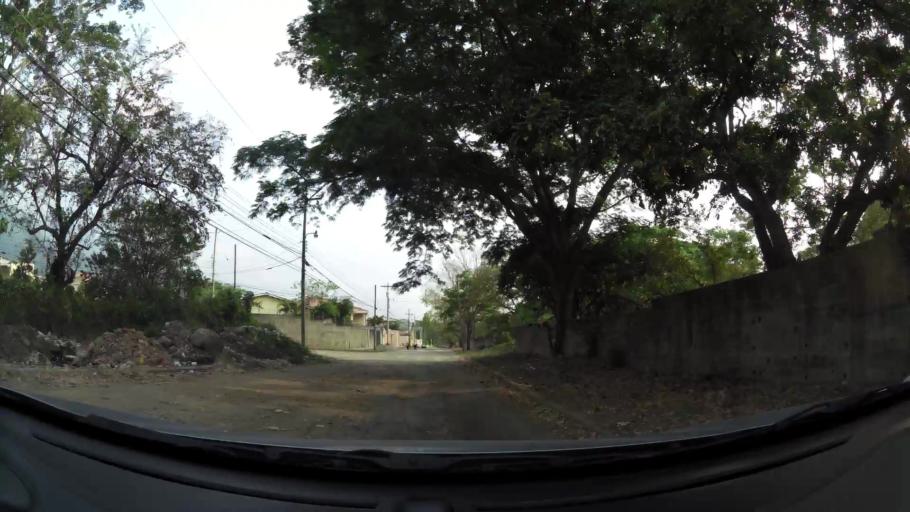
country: HN
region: Cortes
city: Armenta
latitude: 15.4867
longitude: -88.0414
